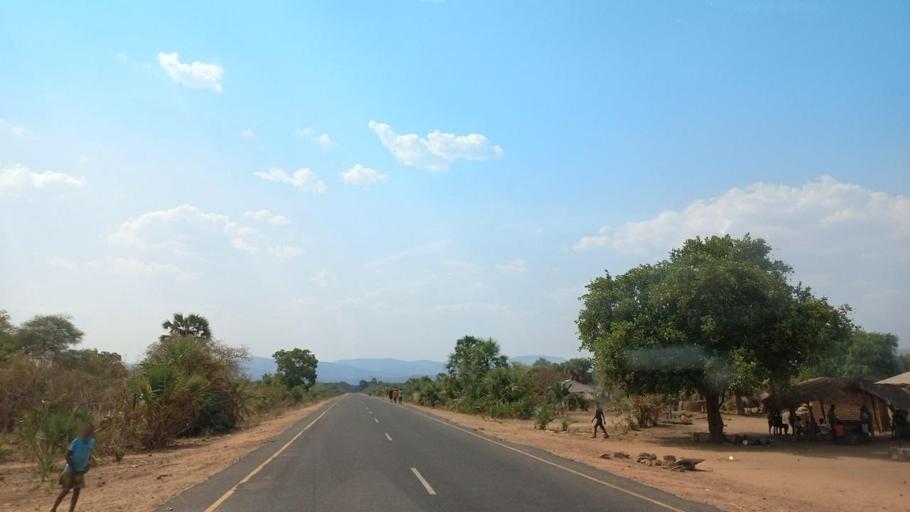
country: ZM
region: Lusaka
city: Luangwa
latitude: -15.1100
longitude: 30.2015
